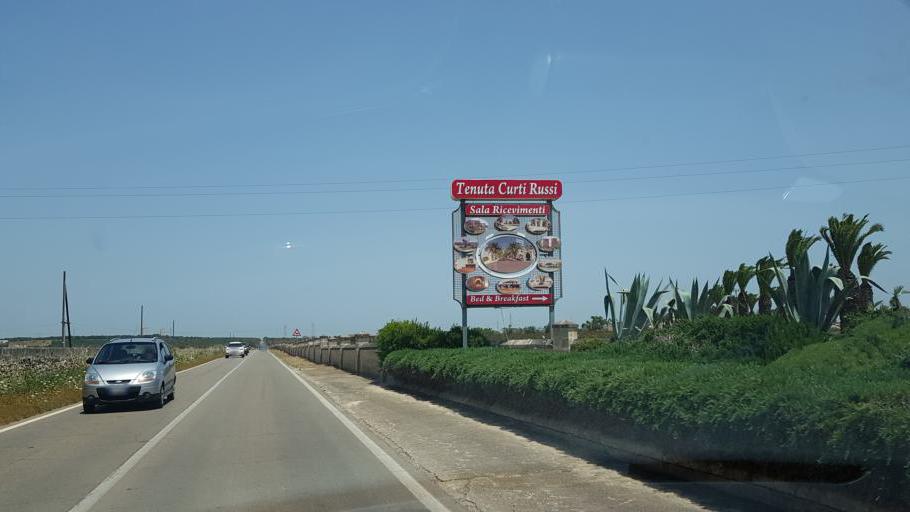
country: IT
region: Apulia
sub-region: Provincia di Lecce
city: Porto Cesareo
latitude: 40.2804
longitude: 17.9061
